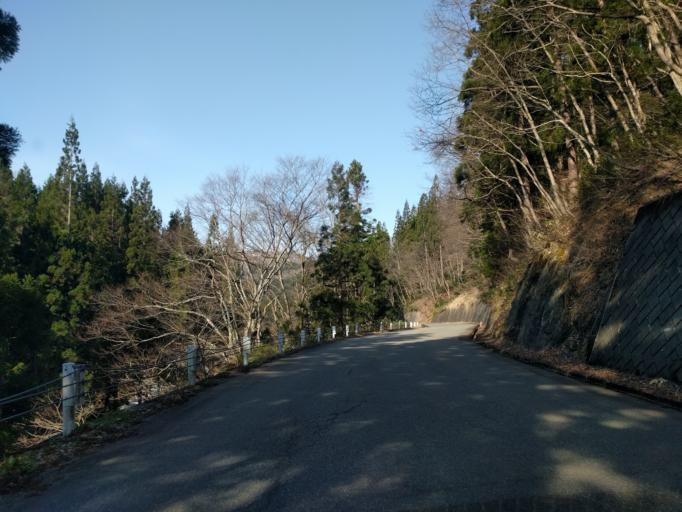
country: JP
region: Niigata
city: Muramatsu
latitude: 37.3889
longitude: 139.4431
